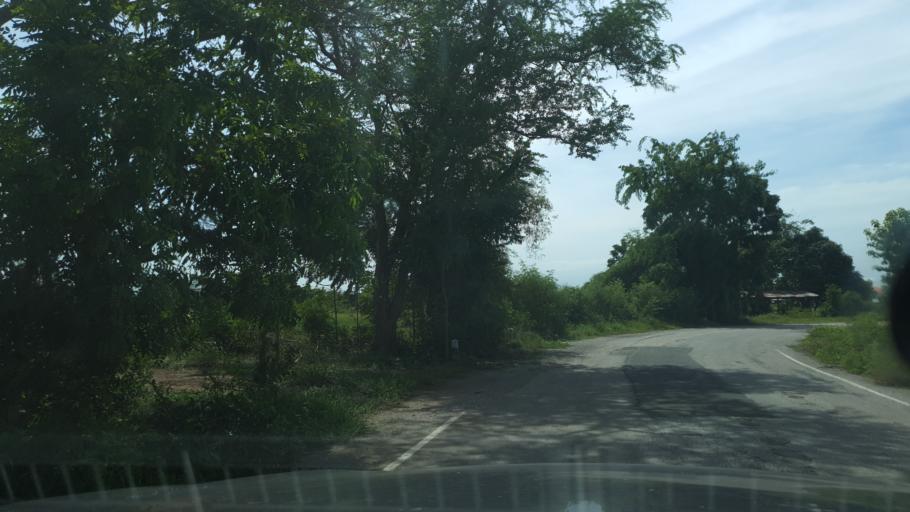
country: TH
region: Sukhothai
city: Si Samrong
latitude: 17.1974
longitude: 99.7254
